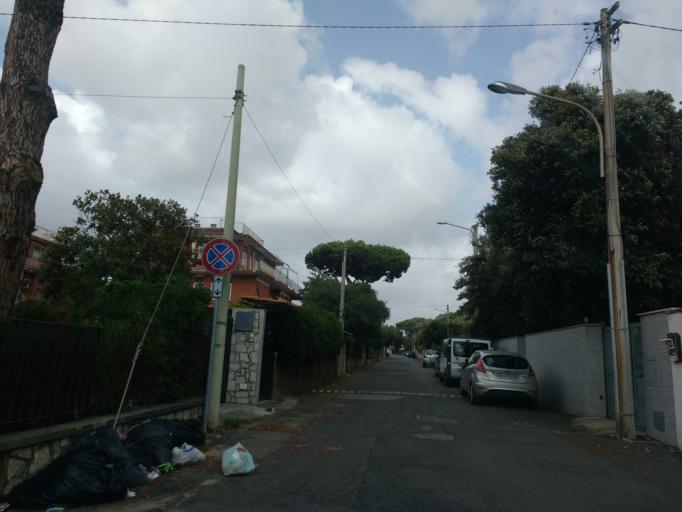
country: IT
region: Latium
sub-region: Citta metropolitana di Roma Capitale
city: Lavinio
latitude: 41.4914
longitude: 12.5906
